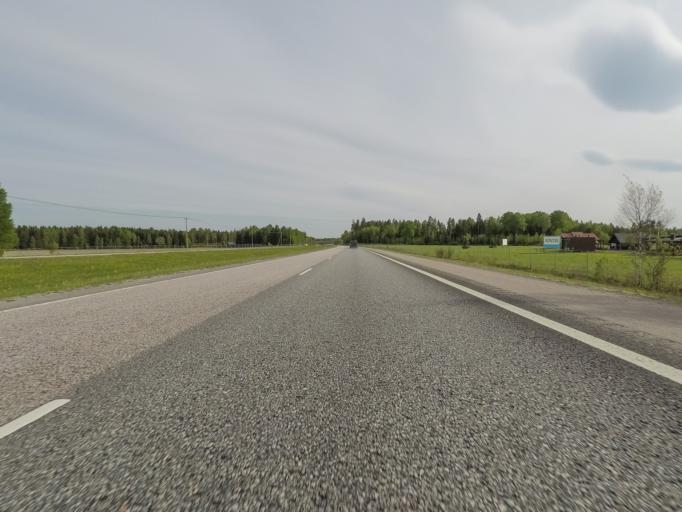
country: FI
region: Uusimaa
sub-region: Helsinki
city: Nurmijaervi
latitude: 60.4800
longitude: 24.8488
